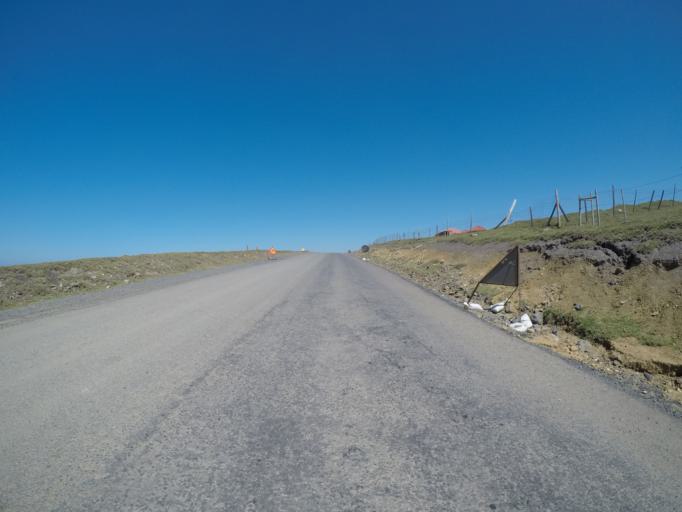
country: ZA
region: Eastern Cape
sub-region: OR Tambo District Municipality
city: Libode
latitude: -31.9910
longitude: 29.1441
